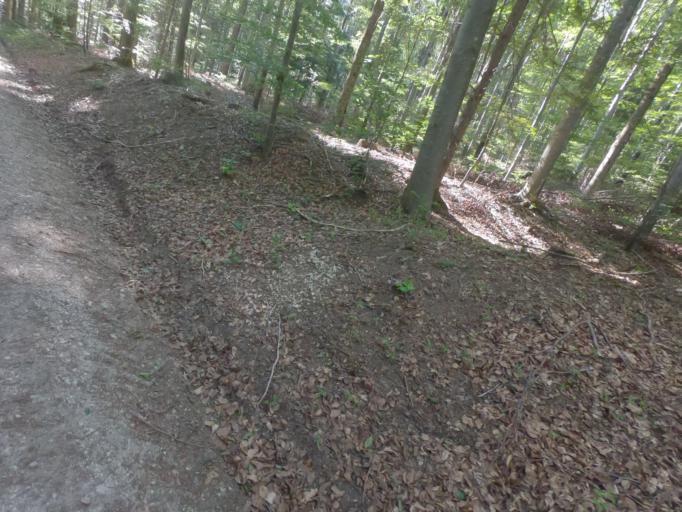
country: CH
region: Solothurn
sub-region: Bezirk Lebern
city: Langendorf
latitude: 47.2375
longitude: 7.5108
